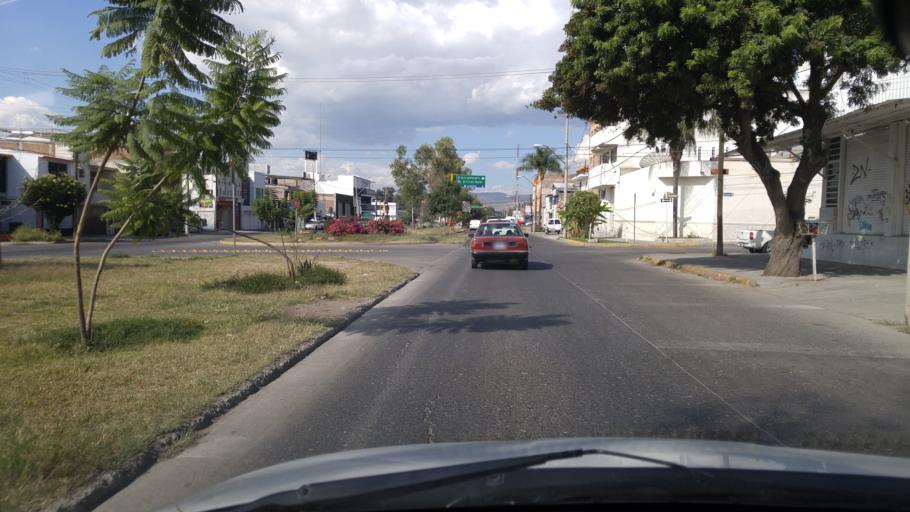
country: MX
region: Guanajuato
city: Leon
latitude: 21.0959
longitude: -101.6413
